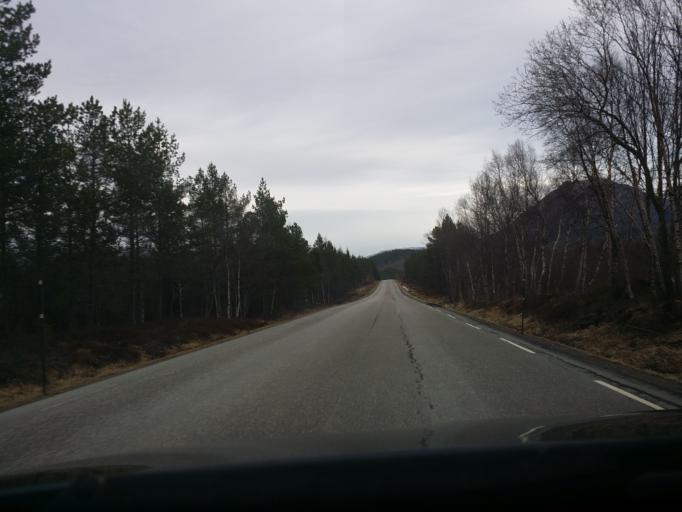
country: NO
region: More og Romsdal
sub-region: Halsa
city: Liaboen
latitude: 63.1236
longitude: 8.3458
